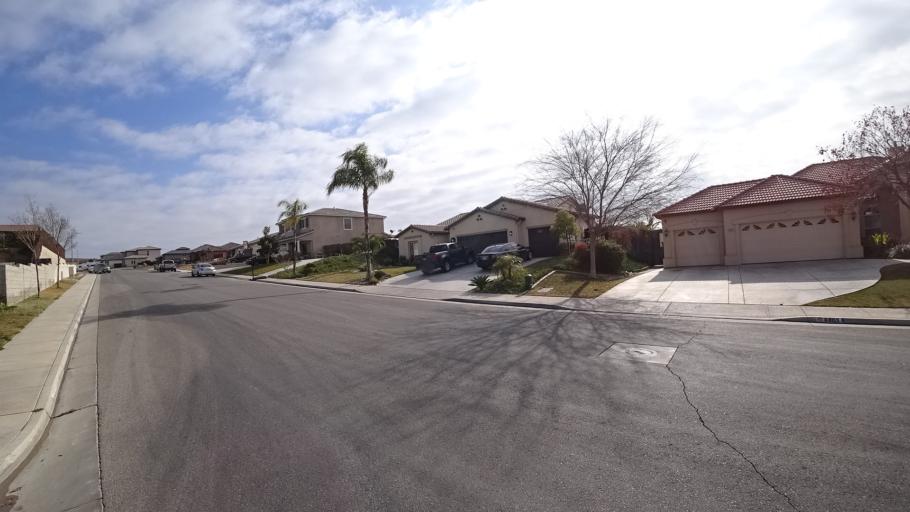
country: US
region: California
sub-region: Kern County
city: Bakersfield
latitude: 35.3875
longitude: -118.9283
